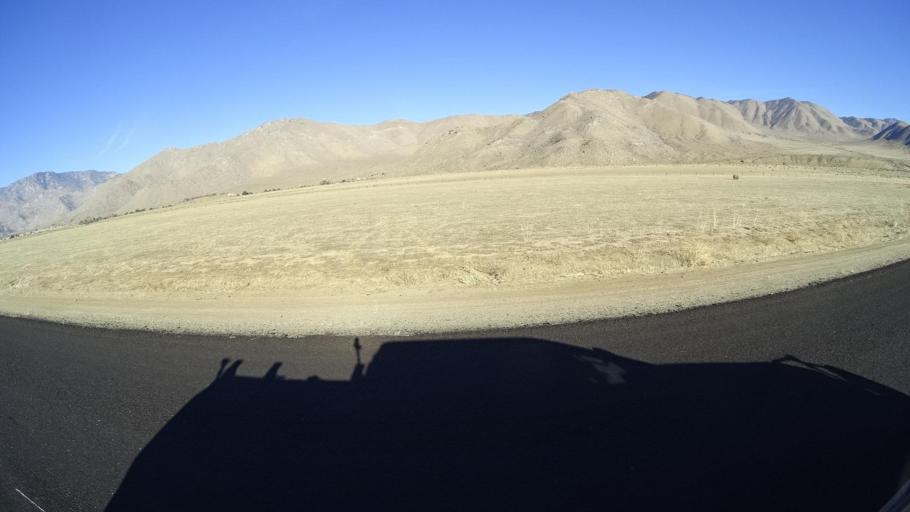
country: US
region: California
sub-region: Kern County
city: Weldon
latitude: 35.6202
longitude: -118.2567
